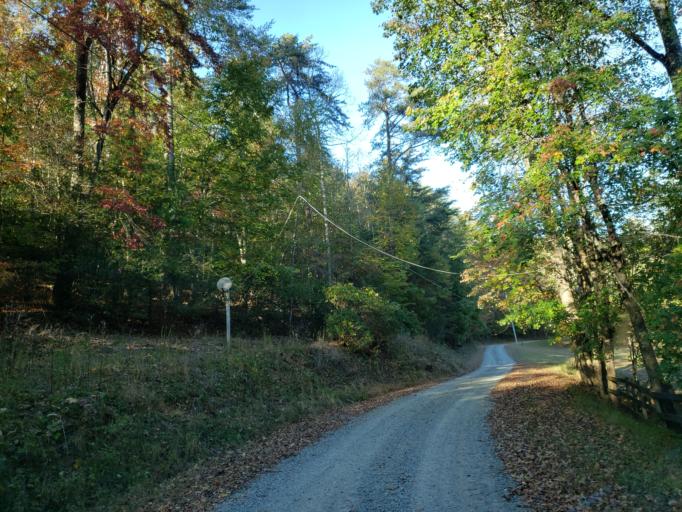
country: US
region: Georgia
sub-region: Fannin County
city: Blue Ridge
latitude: 34.6534
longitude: -84.2587
